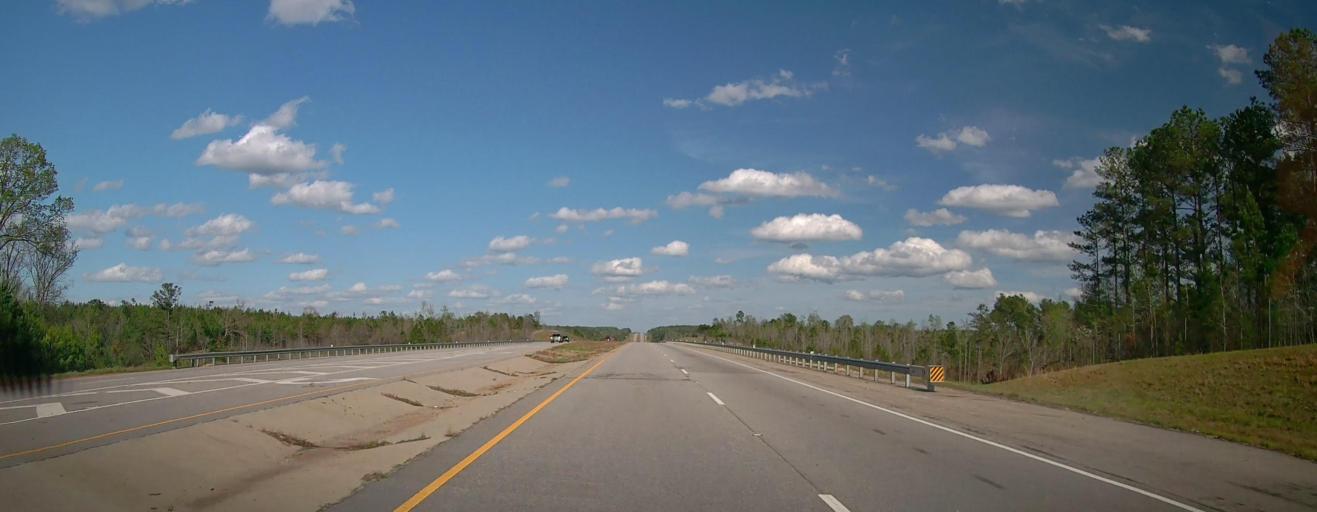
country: US
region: Georgia
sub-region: Baldwin County
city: Hardwick
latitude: 33.0322
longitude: -83.1740
